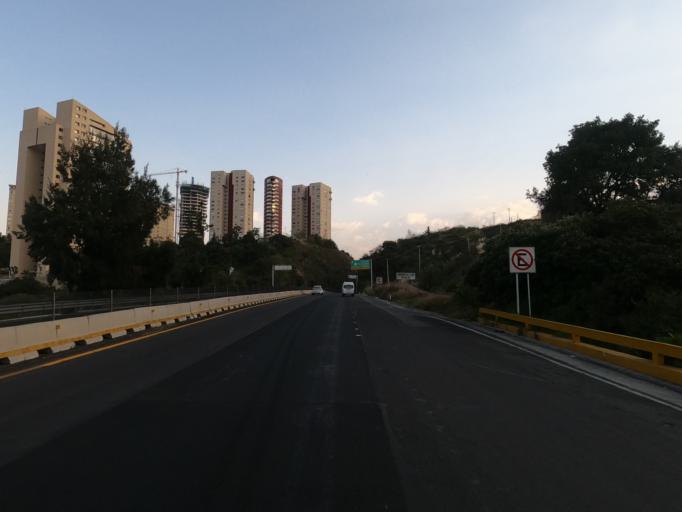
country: MX
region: Mexico
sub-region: Naucalpan de Juarez
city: Ejido el Castillo
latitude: 19.4299
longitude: -99.2961
